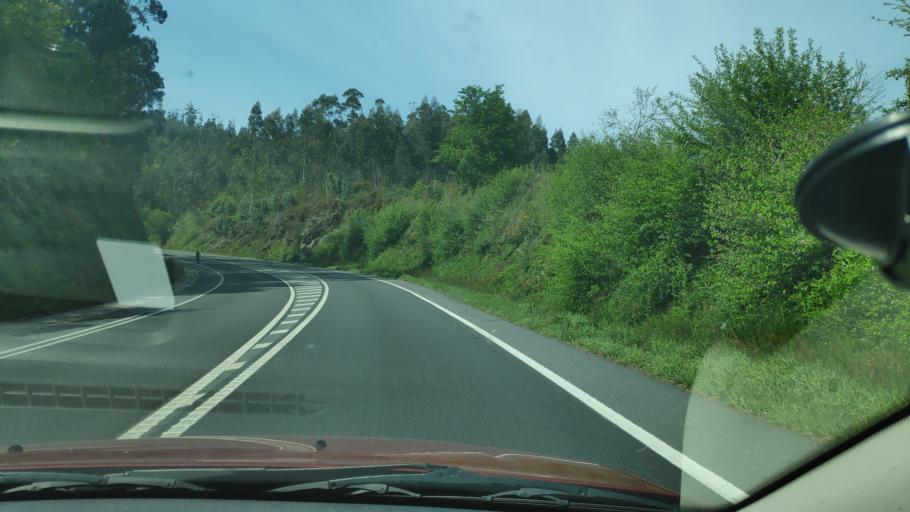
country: ES
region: Galicia
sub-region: Provincia da Coruna
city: Ames
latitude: 42.8792
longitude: -8.6634
